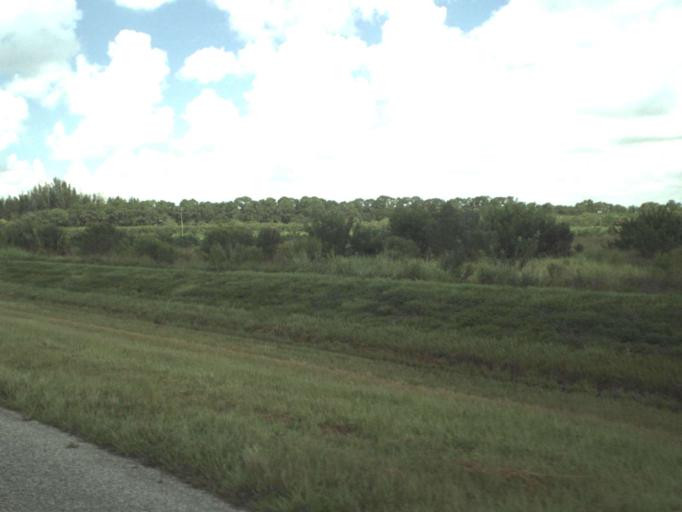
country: US
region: Florida
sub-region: Indian River County
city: West Vero Corridor
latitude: 27.6396
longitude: -80.5483
